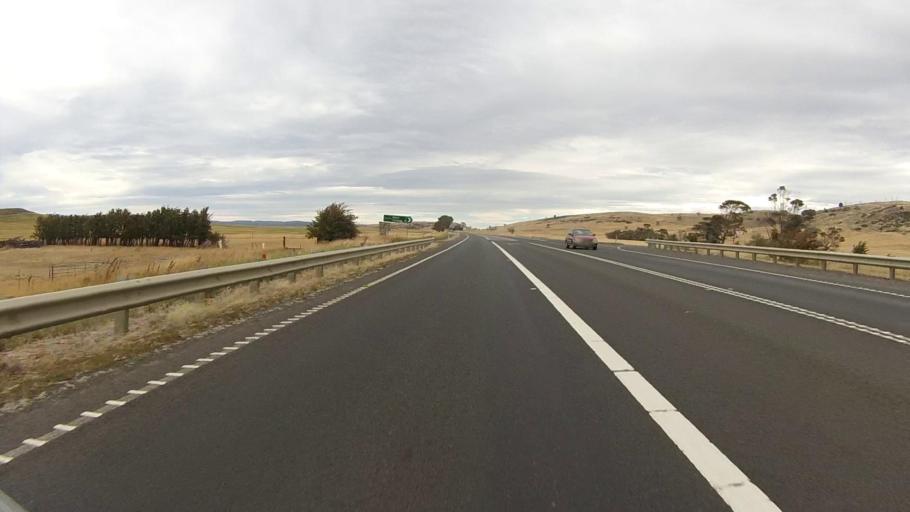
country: AU
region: Tasmania
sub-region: Brighton
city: Bridgewater
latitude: -42.3656
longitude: 147.3353
